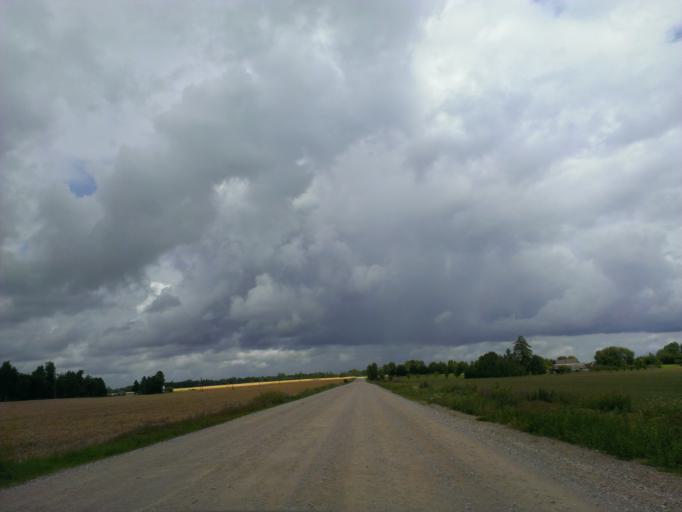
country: LV
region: Sigulda
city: Sigulda
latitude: 57.1871
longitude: 24.9390
